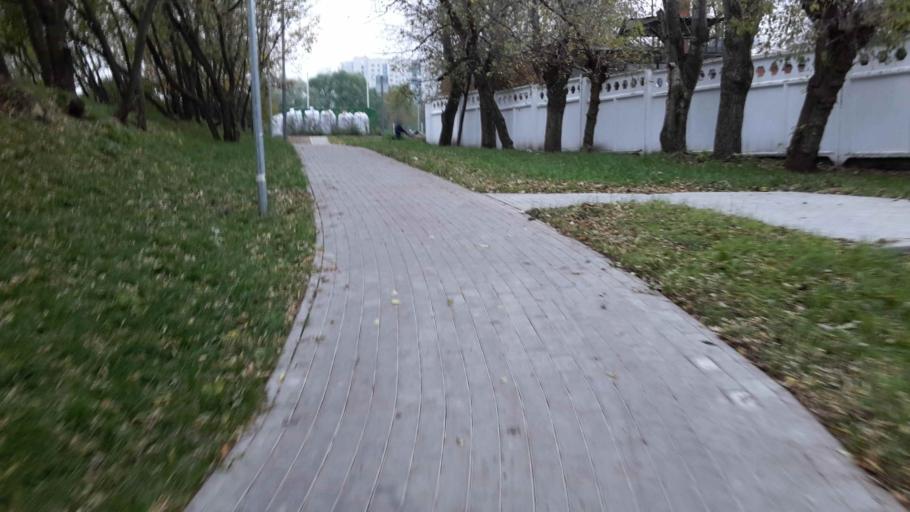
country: RU
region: Moscow
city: Orekhovo-Borisovo
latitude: 55.6299
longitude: 37.7297
